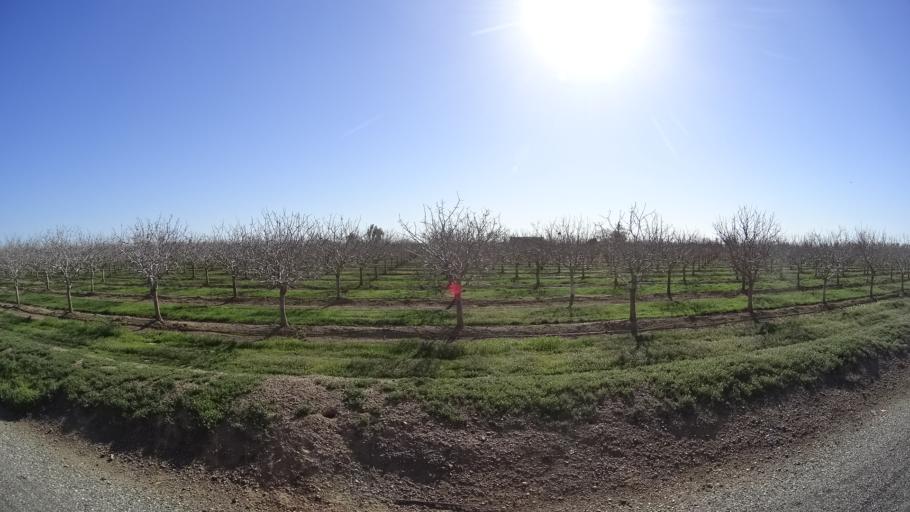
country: US
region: California
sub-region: Glenn County
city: Orland
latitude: 39.7458
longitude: -122.2480
